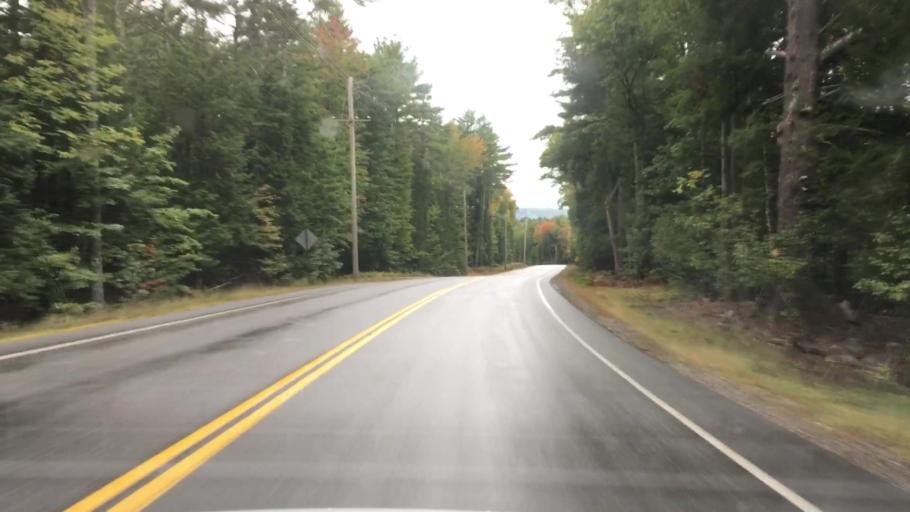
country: US
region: Maine
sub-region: Cumberland County
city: Raymond
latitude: 43.9802
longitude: -70.5331
